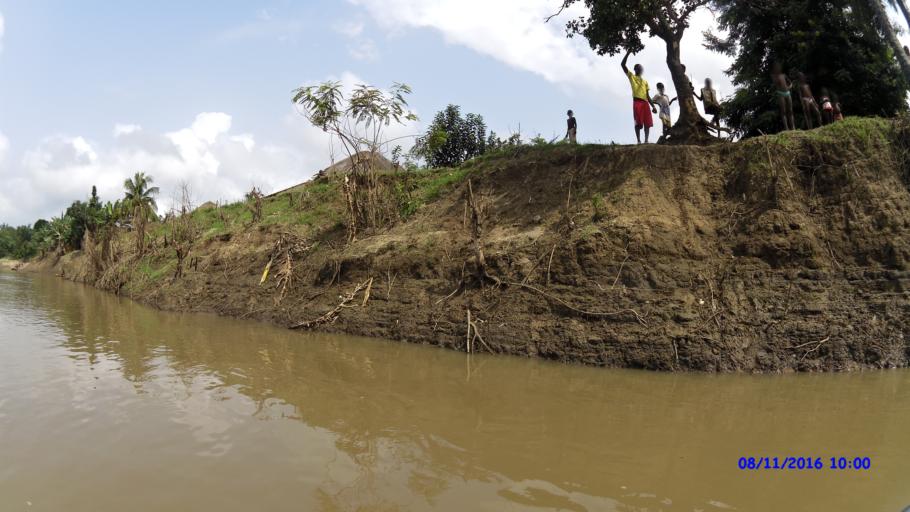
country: BJ
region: Mono
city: Come
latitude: 6.4406
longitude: 1.7629
